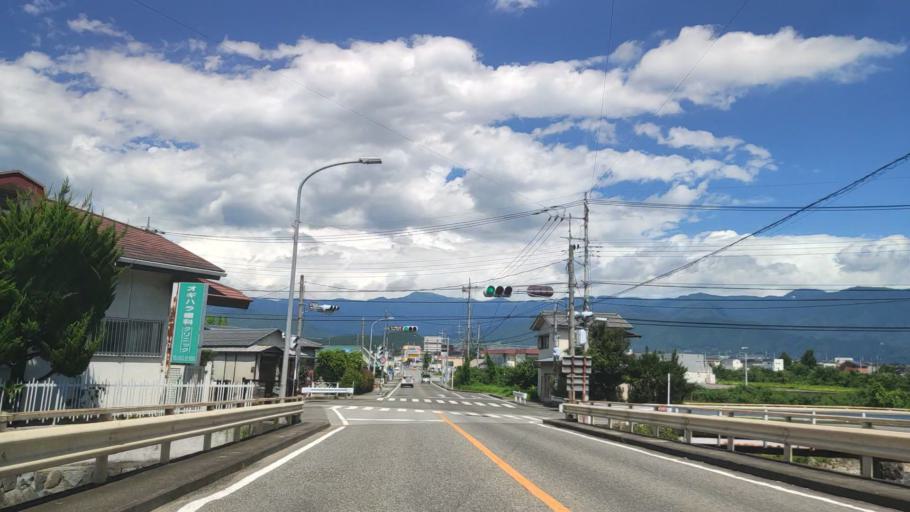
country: JP
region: Yamanashi
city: Enzan
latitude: 35.6985
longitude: 138.6851
